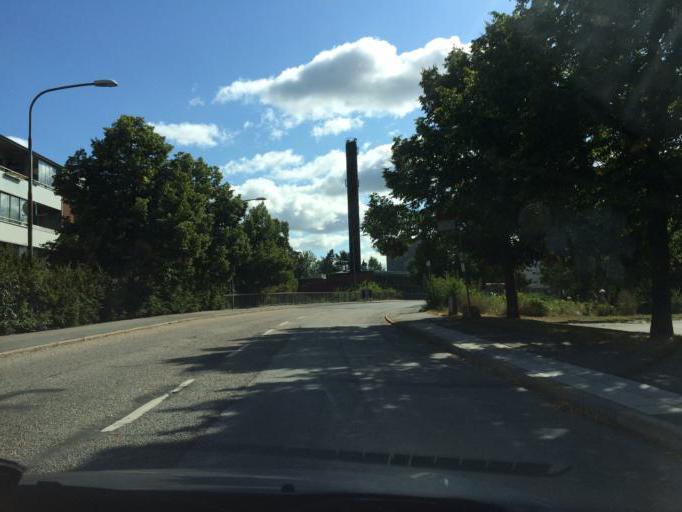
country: SE
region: Stockholm
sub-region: Nacka Kommun
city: Nacka
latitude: 59.2794
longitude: 18.1371
